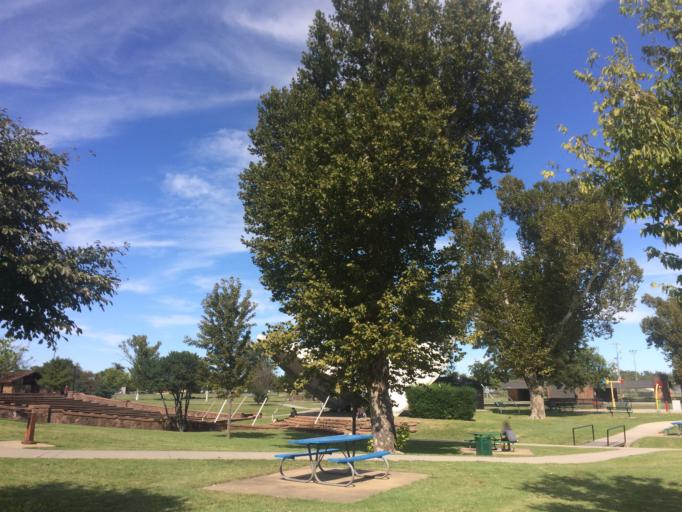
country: US
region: Oklahoma
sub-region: Cleveland County
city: Norman
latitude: 35.2227
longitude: -97.4484
